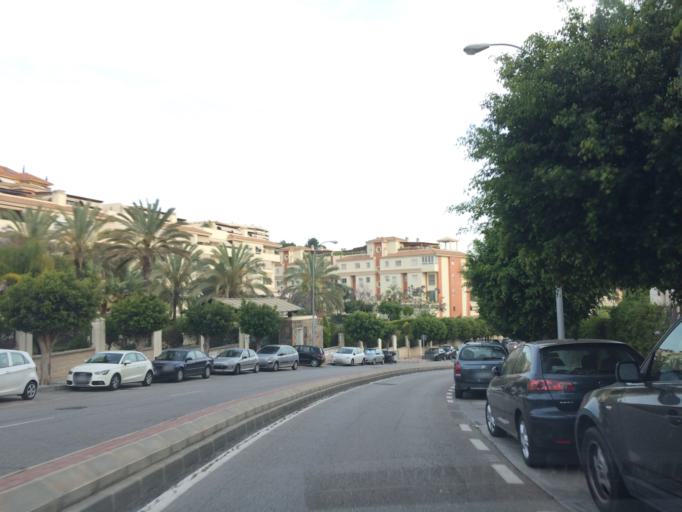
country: ES
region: Andalusia
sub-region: Provincia de Malaga
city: Malaga
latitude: 36.7297
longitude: -4.3895
